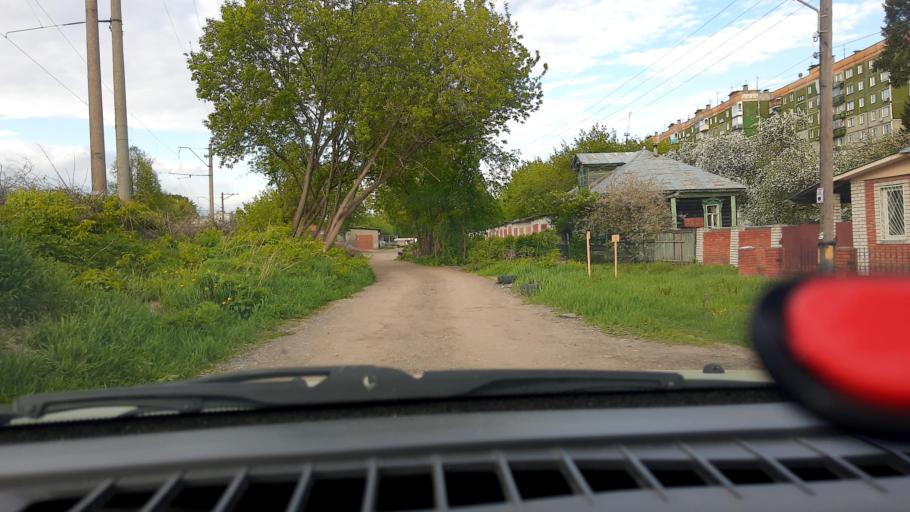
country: RU
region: Nizjnij Novgorod
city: Neklyudovo
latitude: 56.3552
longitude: 43.8534
